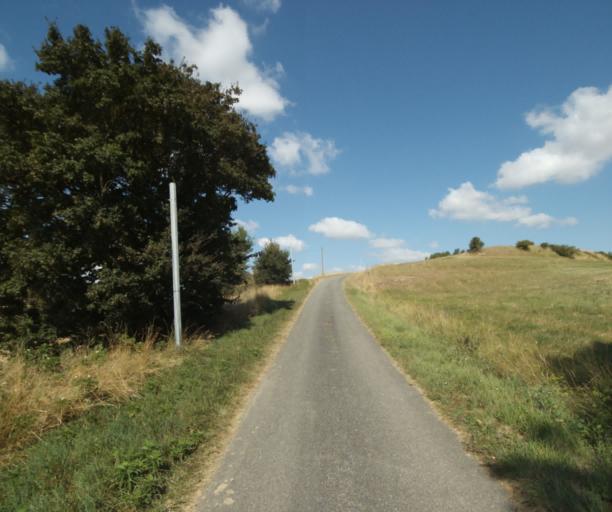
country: FR
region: Midi-Pyrenees
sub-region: Departement de la Haute-Garonne
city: Villefranche-de-Lauragais
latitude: 43.4487
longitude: 1.7759
